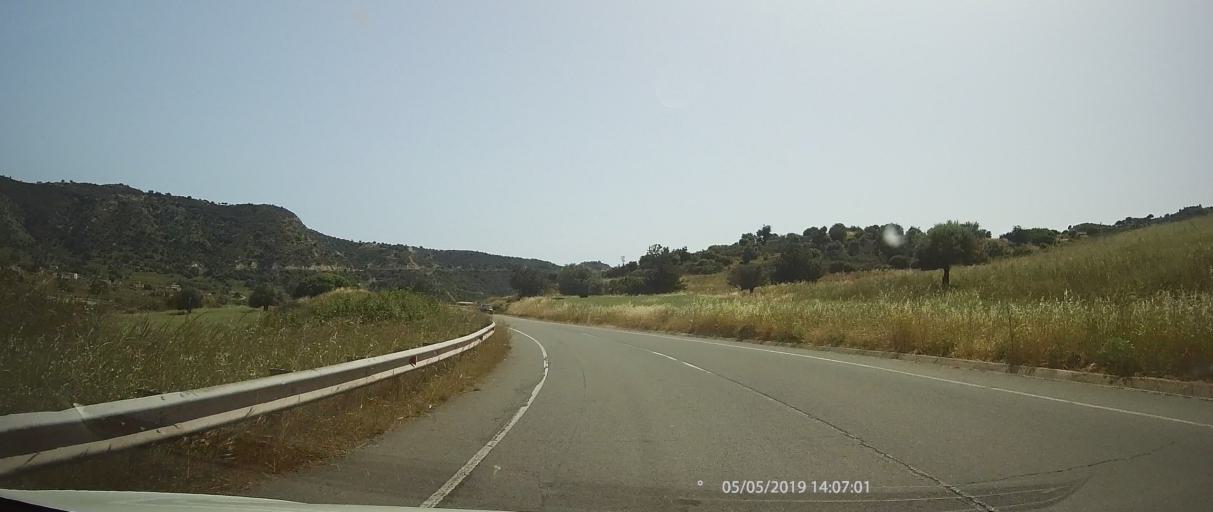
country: CY
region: Limassol
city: Pissouri
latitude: 34.7390
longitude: 32.6017
